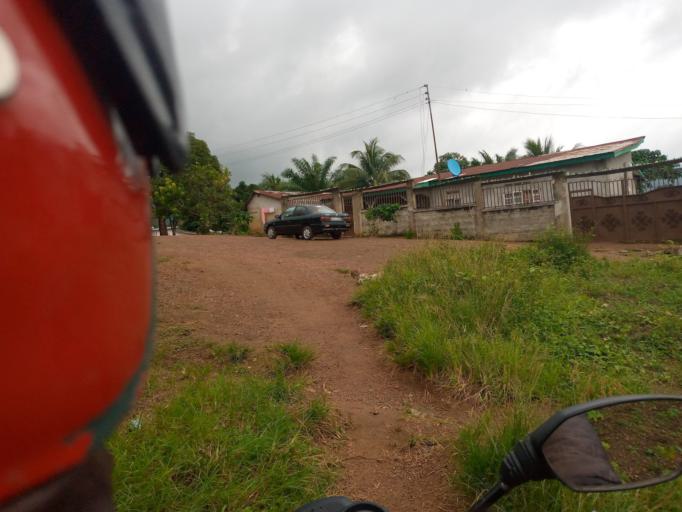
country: SL
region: Eastern Province
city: Kenema
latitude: 7.8486
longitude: -11.2023
